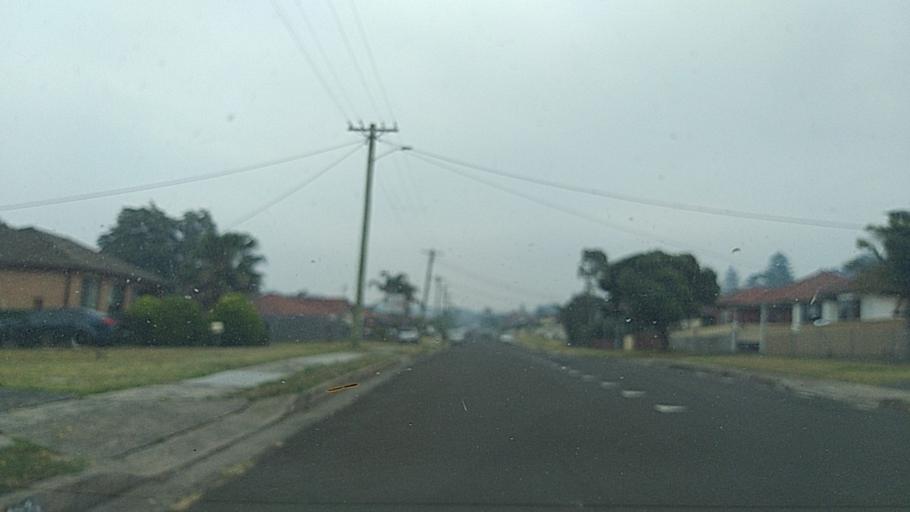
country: AU
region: New South Wales
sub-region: Wollongong
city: Port Kembla
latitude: -34.4880
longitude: 150.8939
